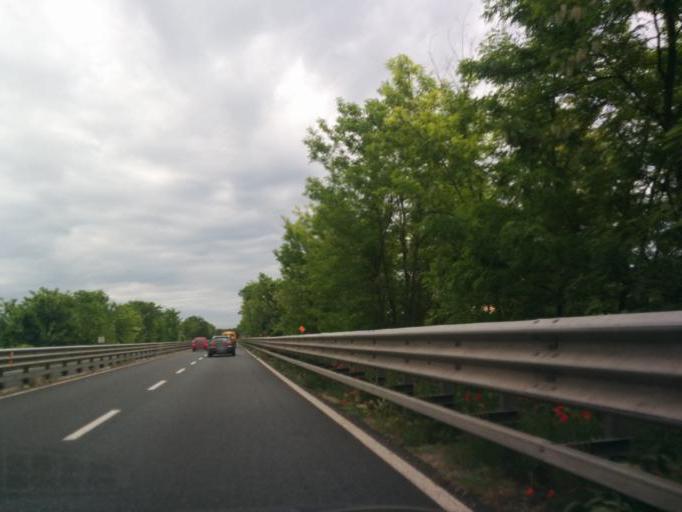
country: IT
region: Tuscany
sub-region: Provincia di Siena
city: Staggia
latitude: 43.4097
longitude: 11.1696
